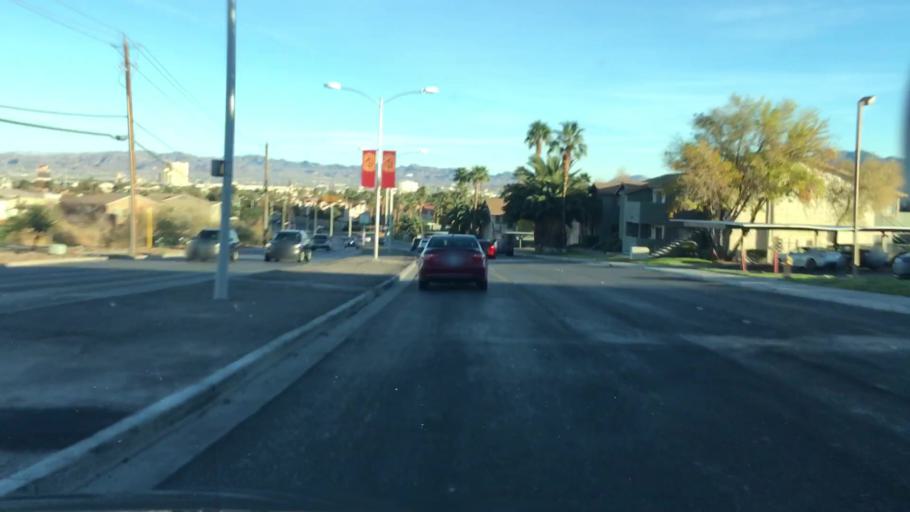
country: US
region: Nevada
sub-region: Clark County
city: Whitney
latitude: 36.0647
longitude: -115.0640
